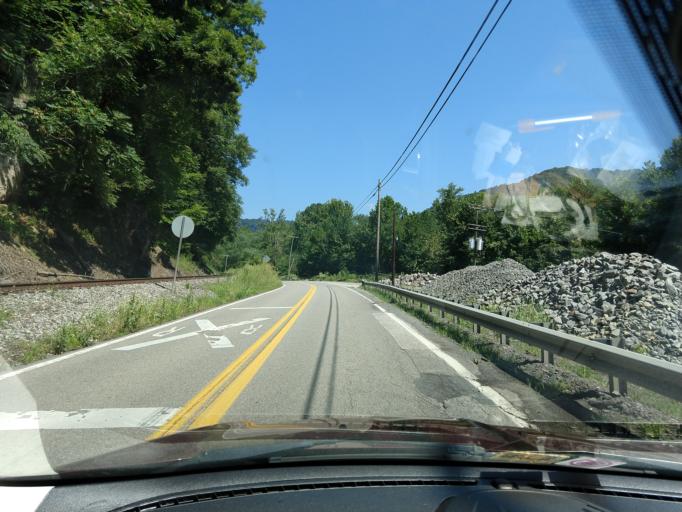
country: US
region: West Virginia
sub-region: Fayette County
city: Ansted
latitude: 38.1421
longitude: -81.2120
